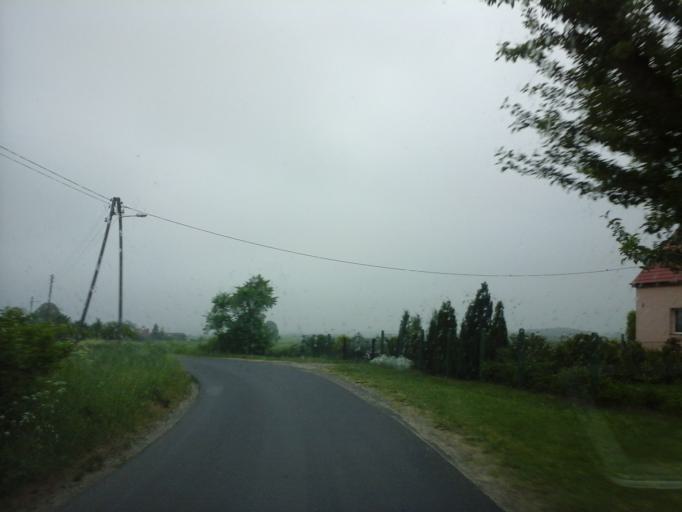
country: PL
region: West Pomeranian Voivodeship
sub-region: Powiat choszczenski
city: Pelczyce
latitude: 53.0224
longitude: 15.3280
